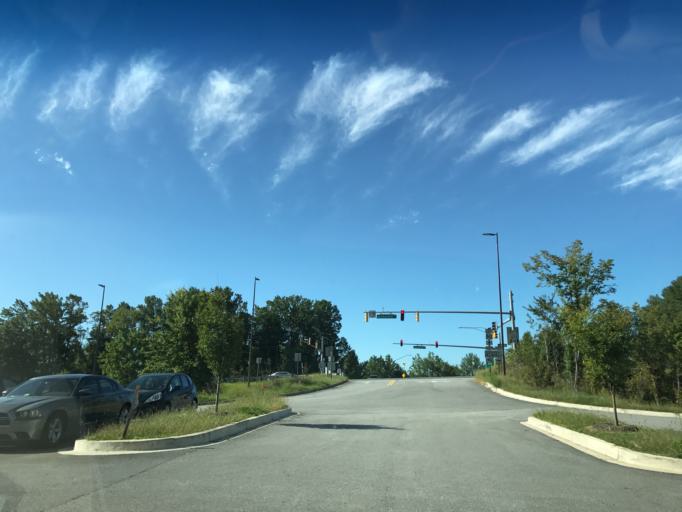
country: US
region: Maryland
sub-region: Anne Arundel County
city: Davidsonville
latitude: 38.9602
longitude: -76.6525
